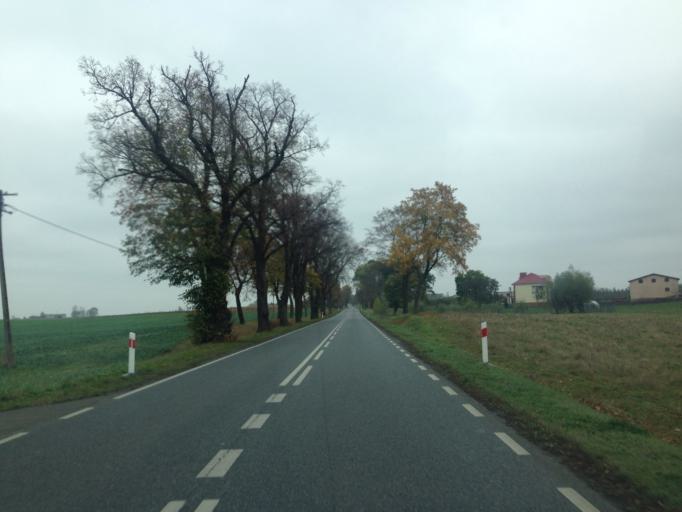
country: PL
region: Kujawsko-Pomorskie
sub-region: Powiat grudziadzki
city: Radzyn Chelminski
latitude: 53.3783
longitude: 19.0066
